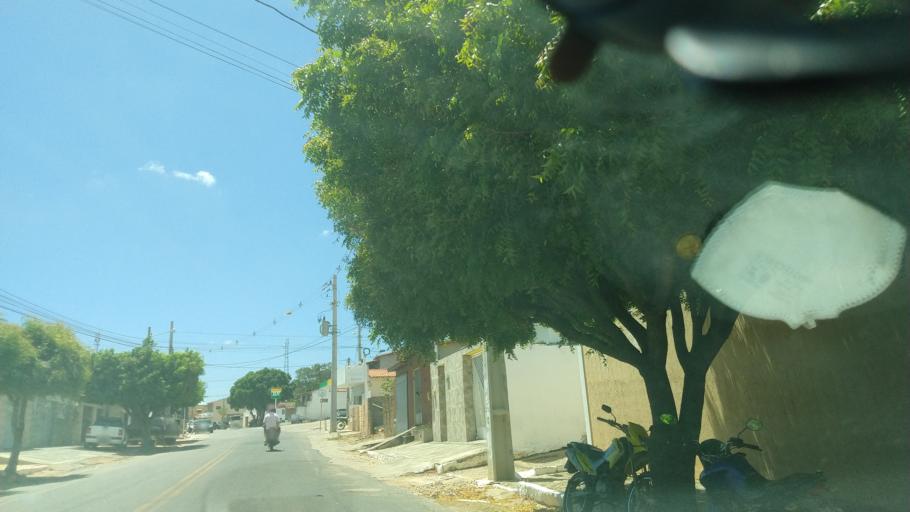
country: BR
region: Rio Grande do Norte
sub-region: Cerro Cora
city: Cerro Cora
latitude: -6.0504
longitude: -36.3528
